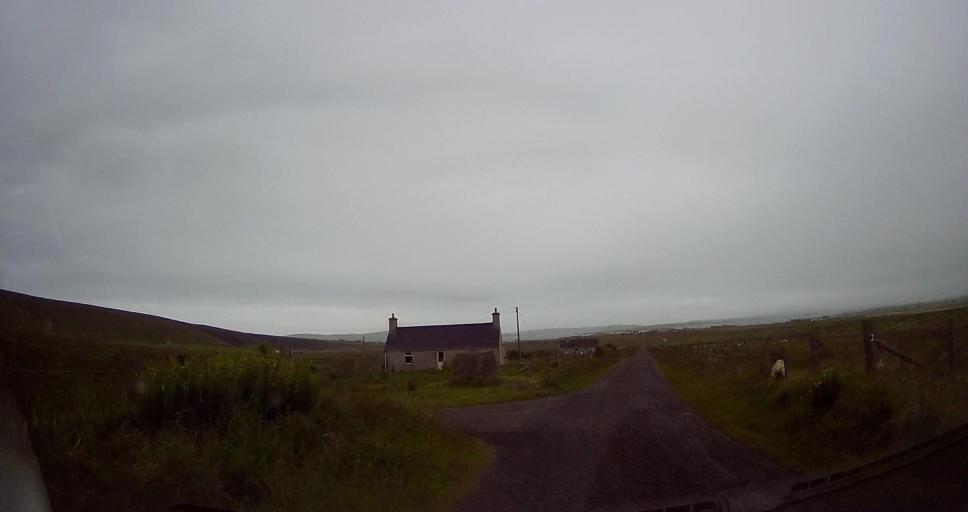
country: GB
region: Scotland
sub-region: Orkney Islands
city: Stromness
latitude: 58.9782
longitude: -3.1720
